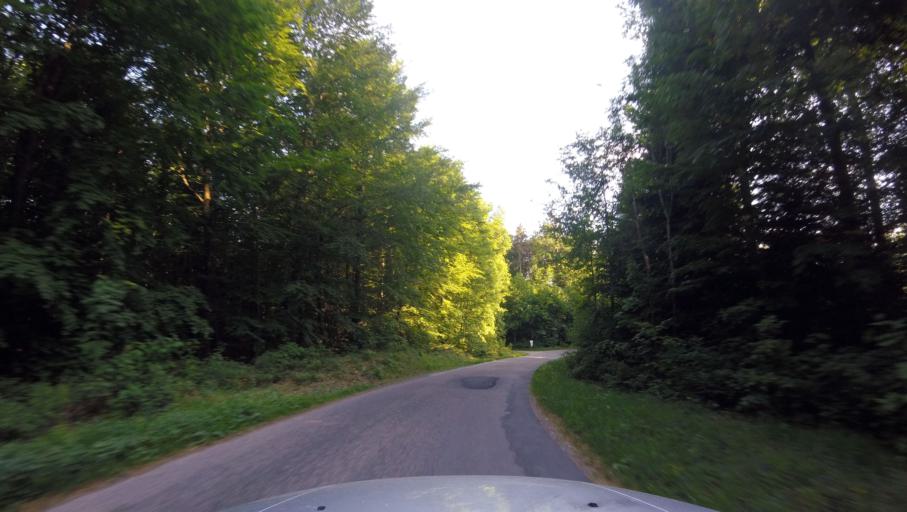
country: DE
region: Baden-Wuerttemberg
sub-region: Regierungsbezirk Stuttgart
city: Aspach
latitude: 49.0125
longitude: 9.4021
